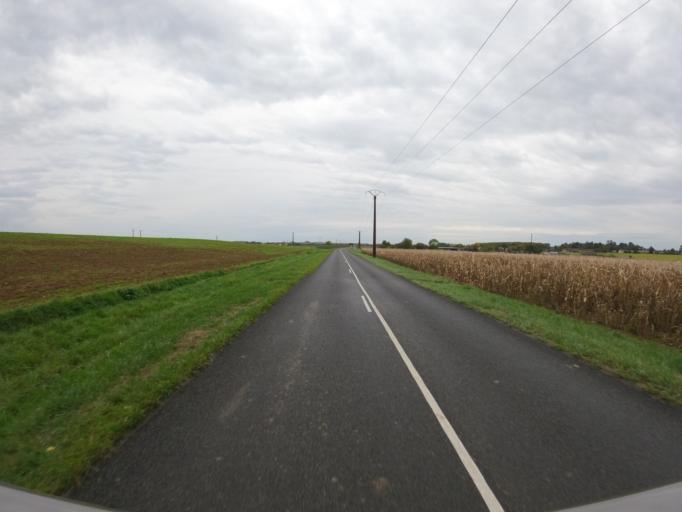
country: FR
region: Ile-de-France
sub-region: Departement de Seine-et-Marne
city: Serris
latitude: 48.8280
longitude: 2.7587
